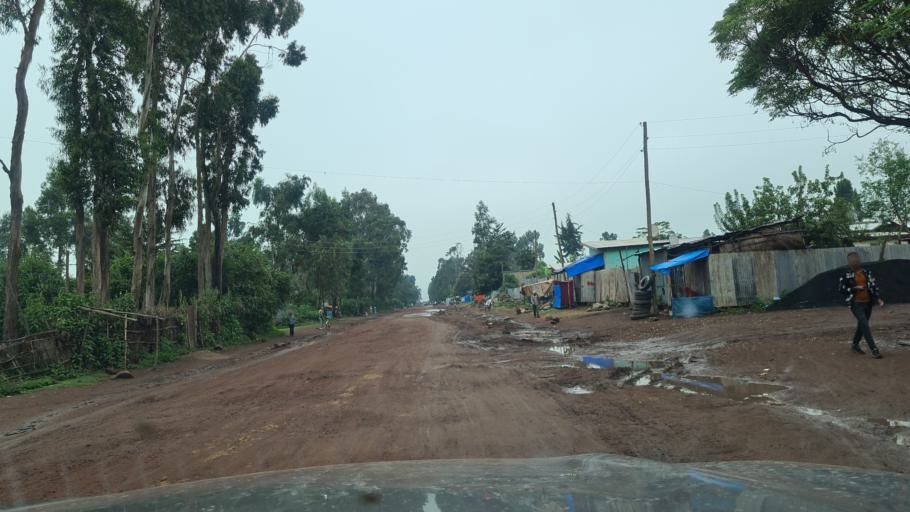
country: ET
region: Oromiya
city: Huruta
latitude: 8.1401
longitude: 39.2375
